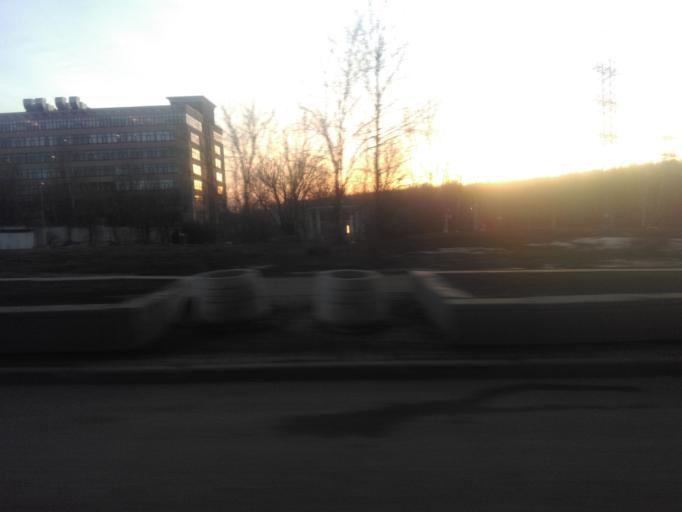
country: RU
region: Moscow
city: Mikhalkovo
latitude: 55.6965
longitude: 37.4237
